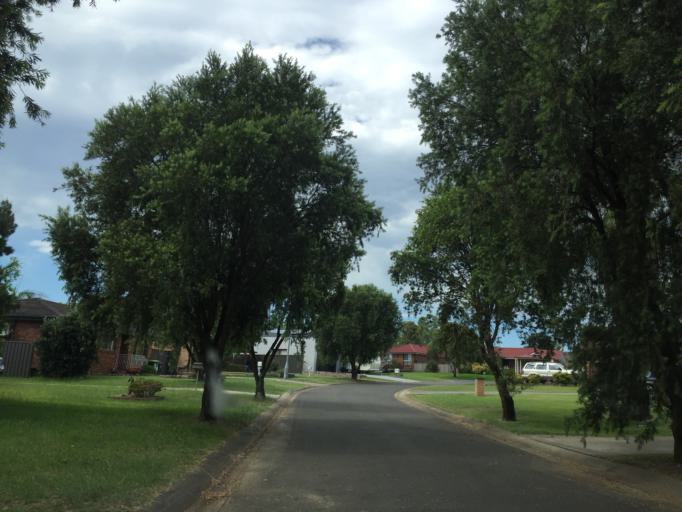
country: AU
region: New South Wales
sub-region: Blacktown
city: Mount Druitt
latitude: -33.8055
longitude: 150.7886
